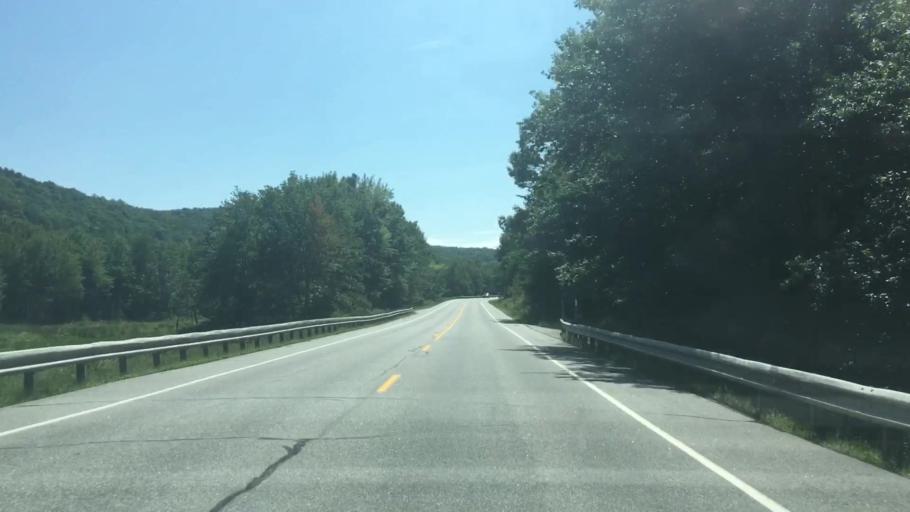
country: US
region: Maine
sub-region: Androscoggin County
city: Sabattus
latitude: 44.1521
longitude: -70.0360
